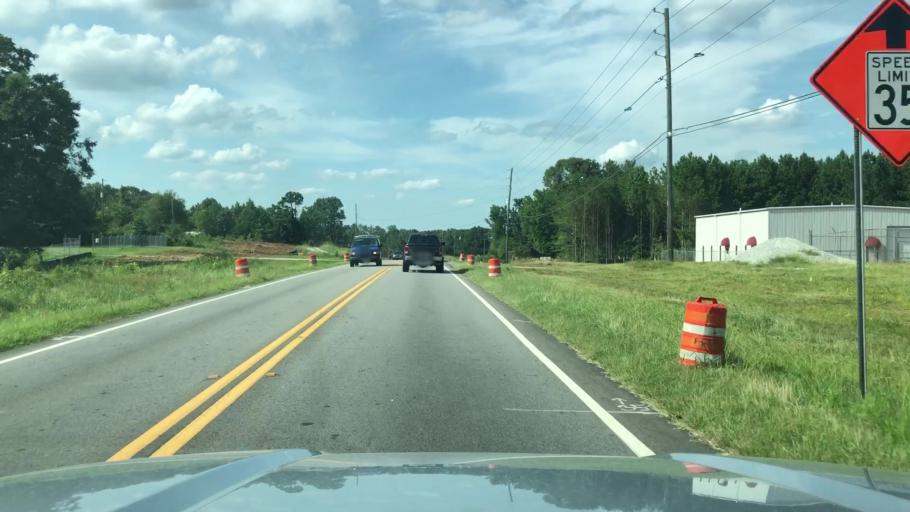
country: US
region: Georgia
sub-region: Paulding County
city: Hiram
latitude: 33.8474
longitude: -84.7569
